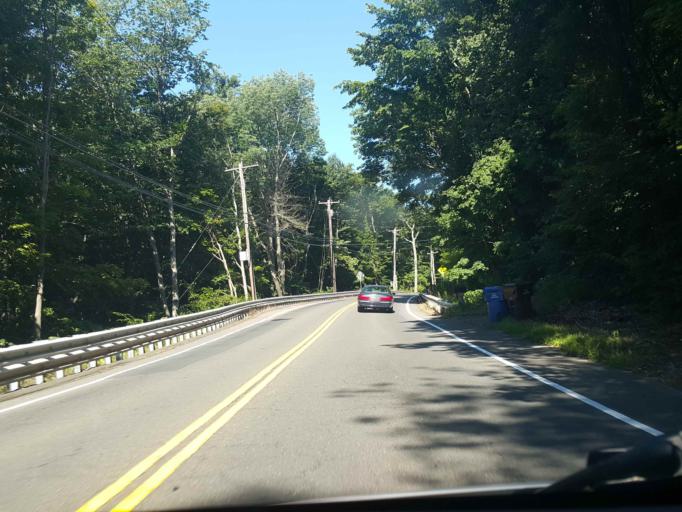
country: US
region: Connecticut
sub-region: New Haven County
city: North Branford
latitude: 41.3197
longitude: -72.7567
